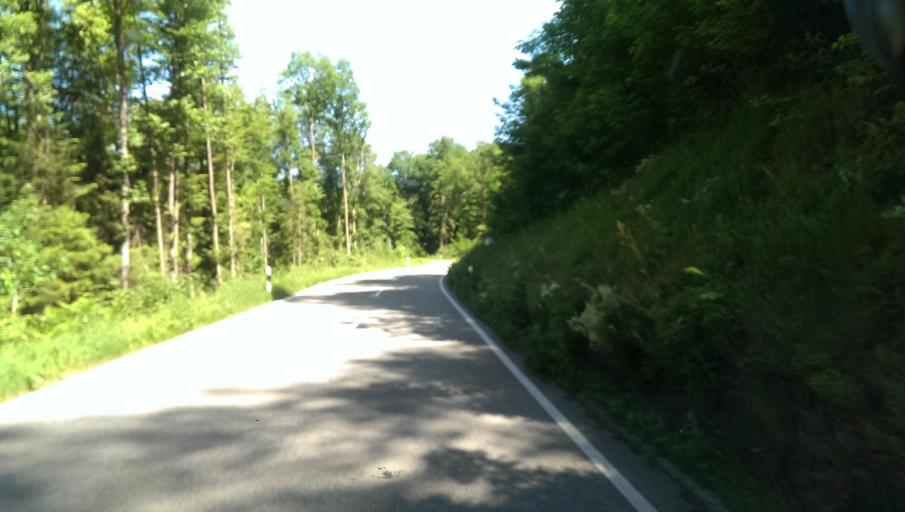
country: DE
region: Rheinland-Pfalz
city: Fischbach
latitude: 49.0817
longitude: 7.7357
